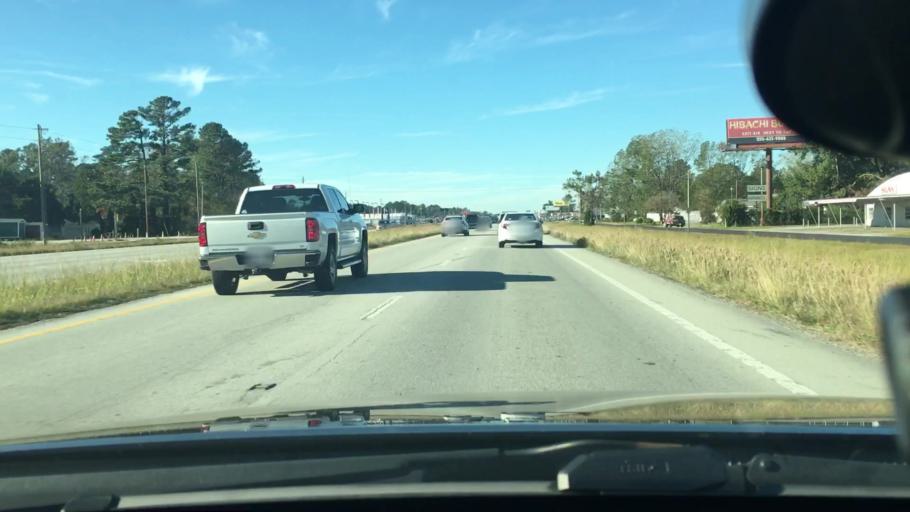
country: US
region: North Carolina
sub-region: Craven County
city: James City
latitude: 35.0658
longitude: -77.0228
